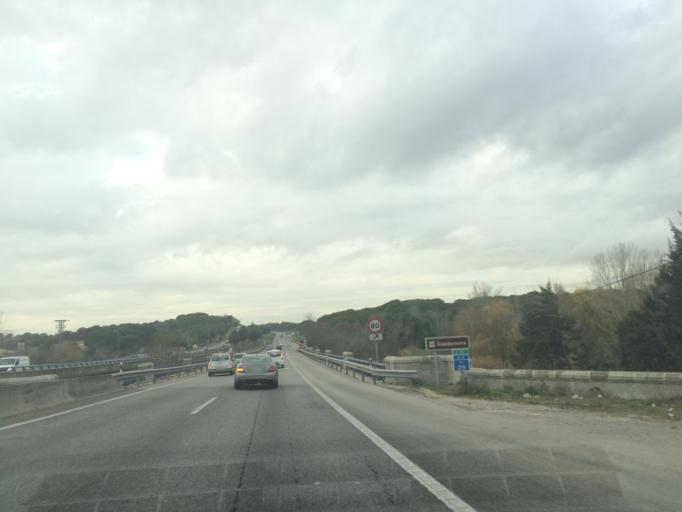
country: ES
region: Madrid
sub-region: Provincia de Madrid
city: Arroyomolinos
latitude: 40.2986
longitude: -3.9404
